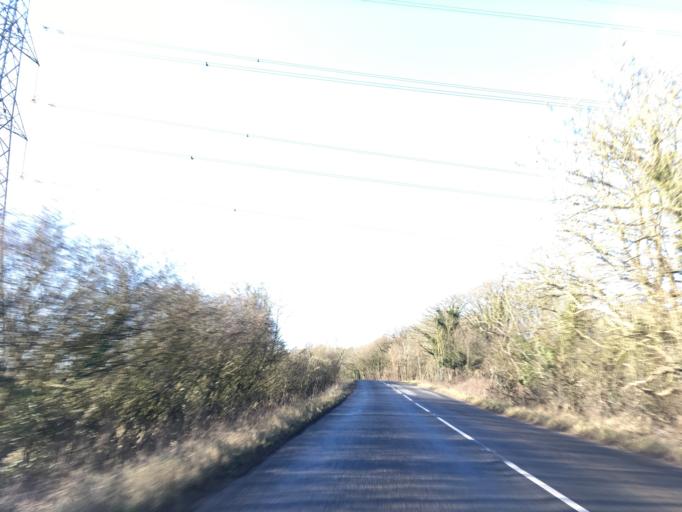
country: GB
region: England
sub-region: Wiltshire
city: Hankerton
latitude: 51.6024
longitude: -2.0097
